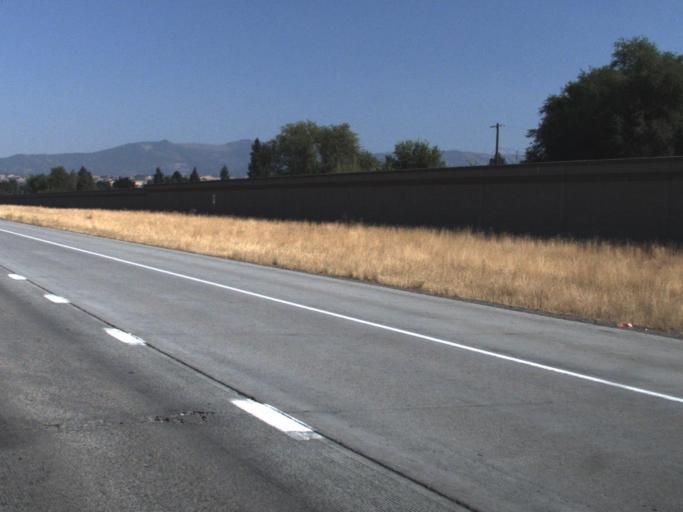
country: US
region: Washington
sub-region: Spokane County
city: Veradale
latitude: 47.6656
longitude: -117.1655
